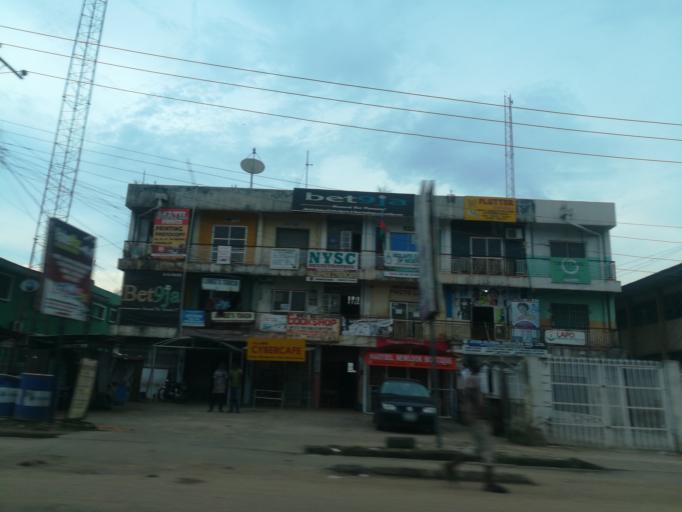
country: NG
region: Oyo
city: Ibadan
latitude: 7.4429
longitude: 3.9068
